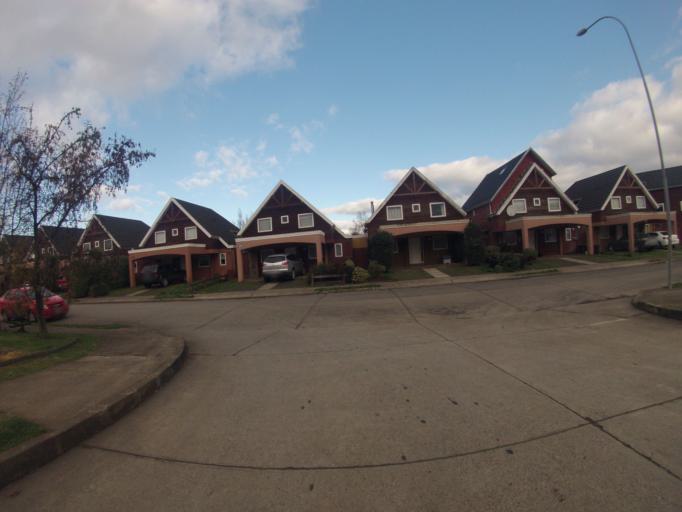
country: CL
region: Araucania
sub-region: Provincia de Cautin
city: Temuco
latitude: -38.7345
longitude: -72.6467
